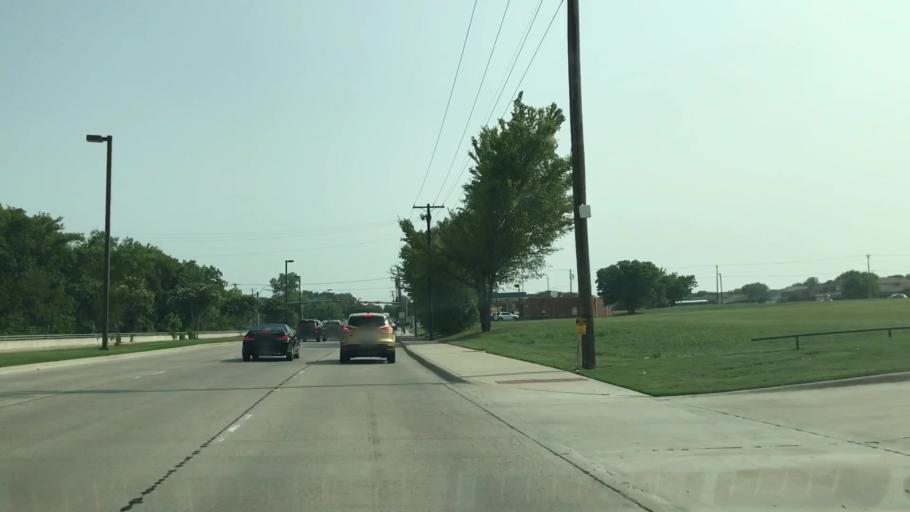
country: US
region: Texas
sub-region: Dallas County
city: Rowlett
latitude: 32.8959
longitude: -96.5696
